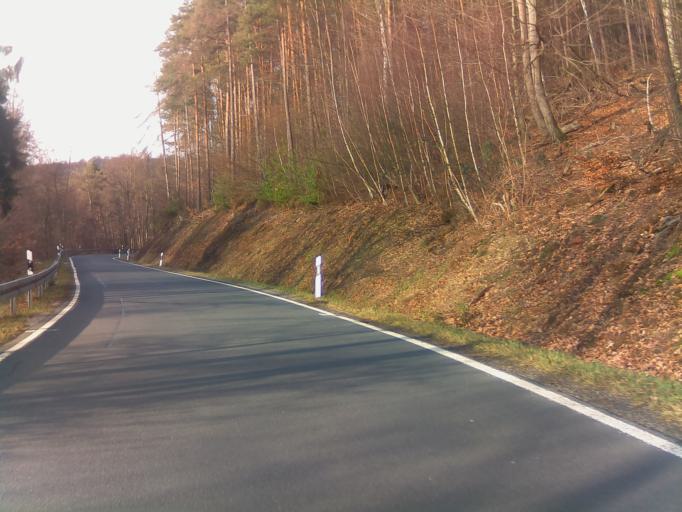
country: DE
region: Bavaria
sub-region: Regierungsbezirk Unterfranken
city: Monchberg
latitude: 49.7932
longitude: 9.3100
